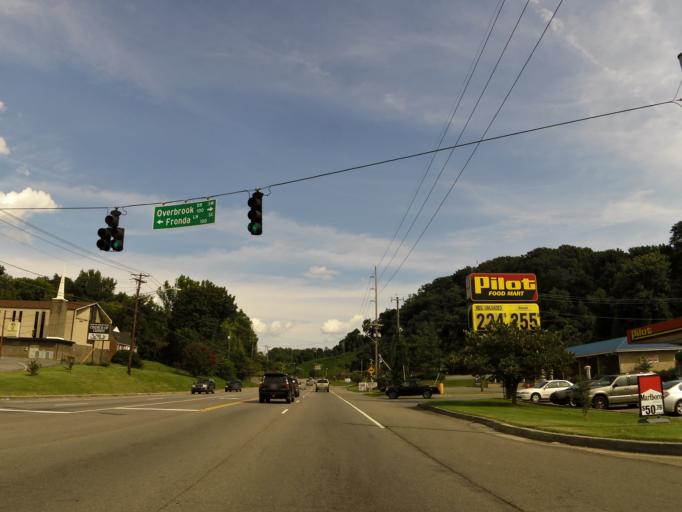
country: US
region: Tennessee
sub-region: Knox County
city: Knoxville
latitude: 35.9315
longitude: -83.9023
